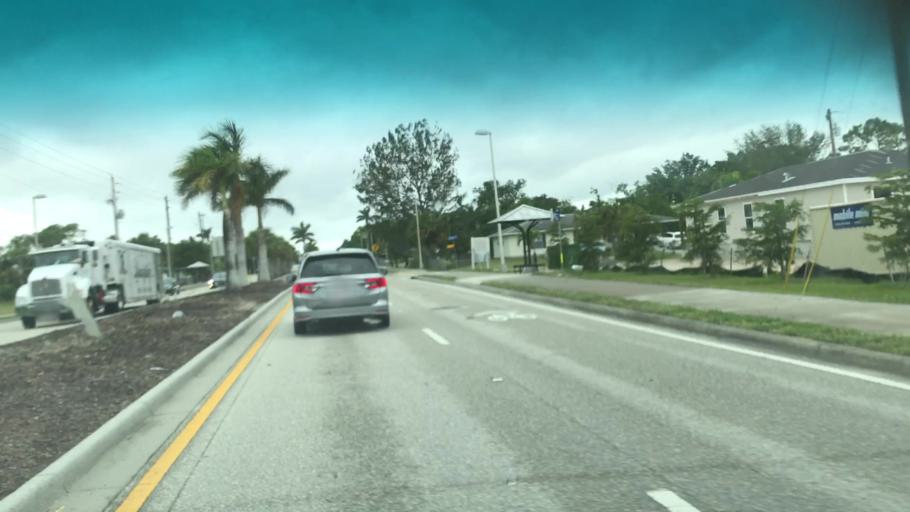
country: US
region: Florida
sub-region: Lee County
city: Harlem Heights
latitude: 26.5183
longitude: -81.9278
